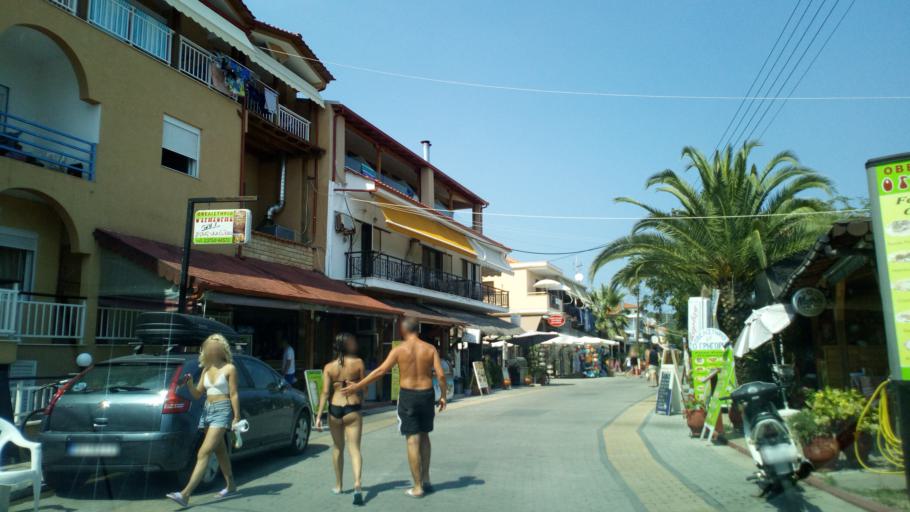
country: GR
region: Central Macedonia
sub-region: Nomos Chalkidikis
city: Sarti
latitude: 40.0954
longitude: 23.9793
